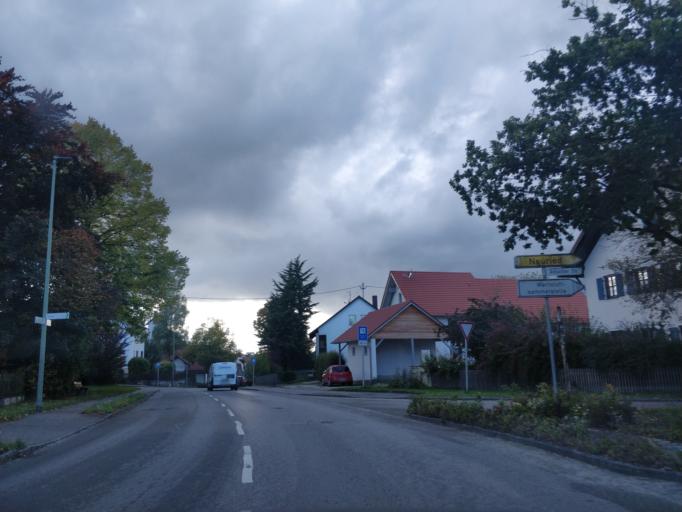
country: DE
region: Bavaria
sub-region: Swabia
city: Ried
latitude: 48.2916
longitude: 11.0488
